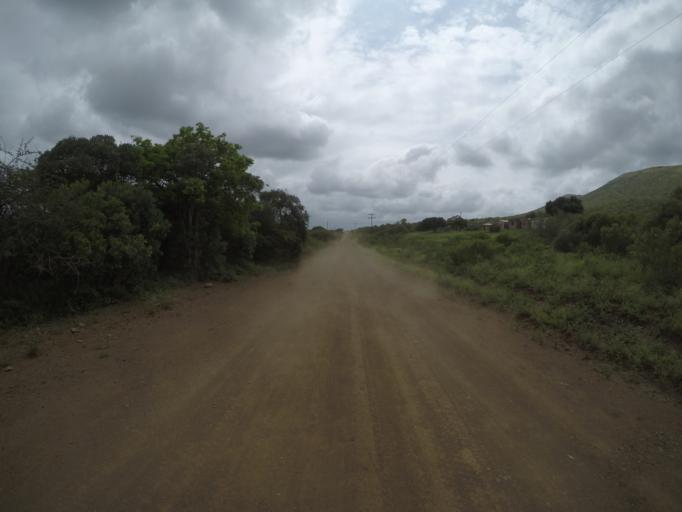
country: ZA
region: KwaZulu-Natal
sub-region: uThungulu District Municipality
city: Empangeni
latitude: -28.5749
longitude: 31.8714
